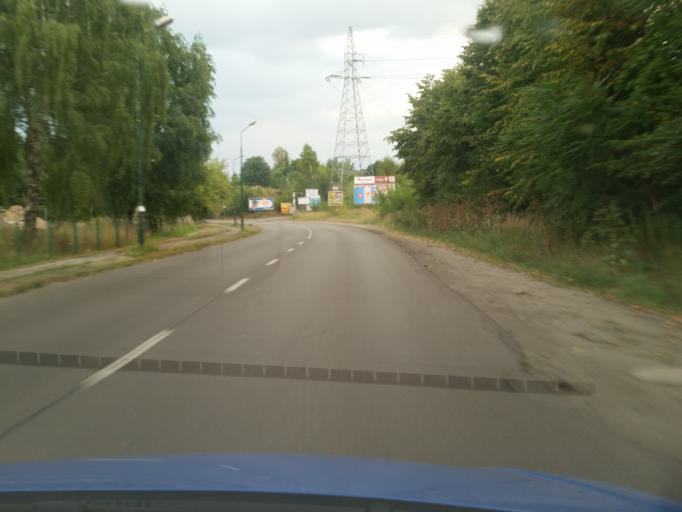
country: PL
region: Silesian Voivodeship
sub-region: Sosnowiec
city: Sosnowiec
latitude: 50.2615
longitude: 19.1380
